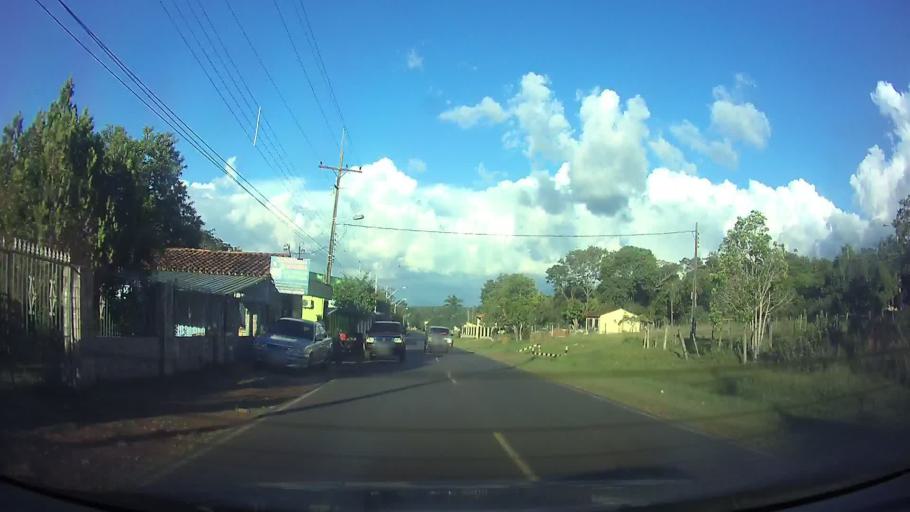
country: PY
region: Cordillera
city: Emboscada
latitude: -25.1919
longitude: -57.3111
